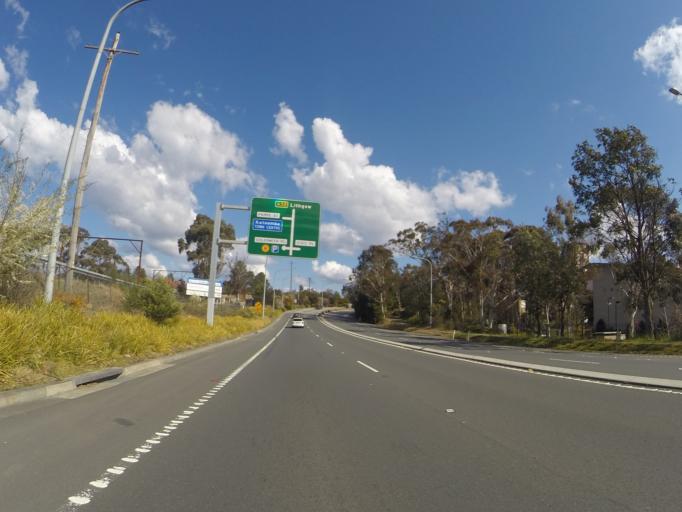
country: AU
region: New South Wales
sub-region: Blue Mountains Municipality
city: Katoomba
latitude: -33.7100
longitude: 150.3158
